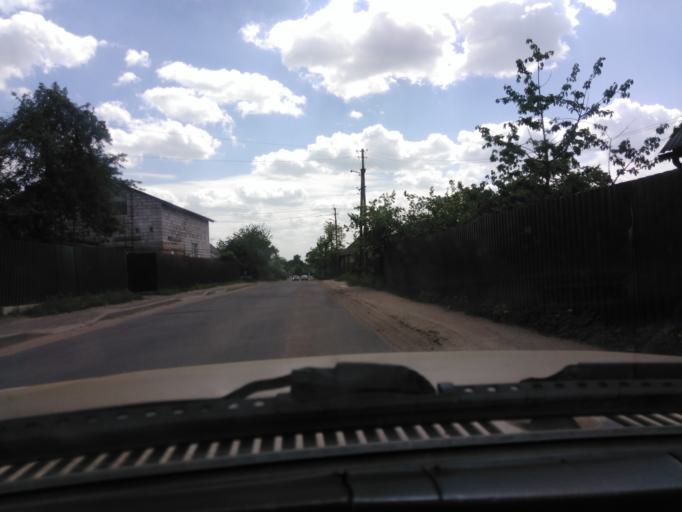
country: BY
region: Mogilev
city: Mahilyow
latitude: 53.9357
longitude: 30.3227
